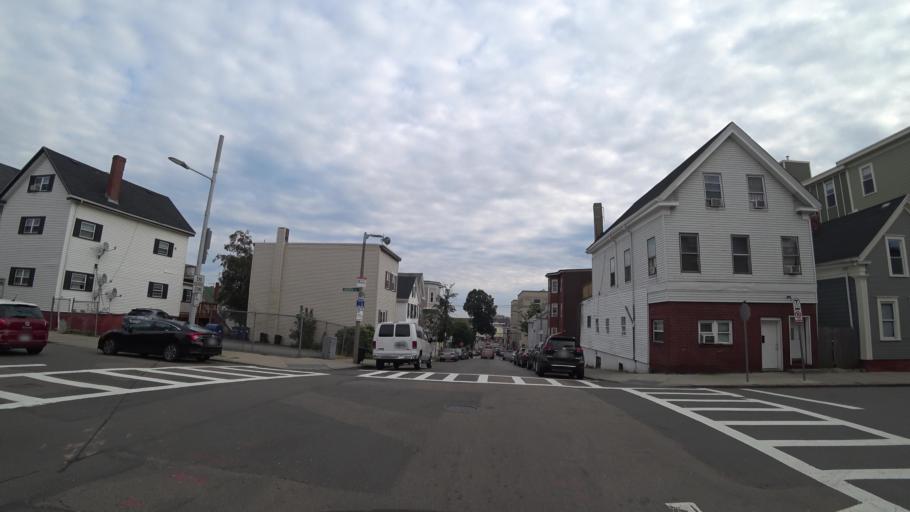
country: US
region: Massachusetts
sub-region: Suffolk County
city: Chelsea
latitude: 42.3780
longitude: -71.0372
